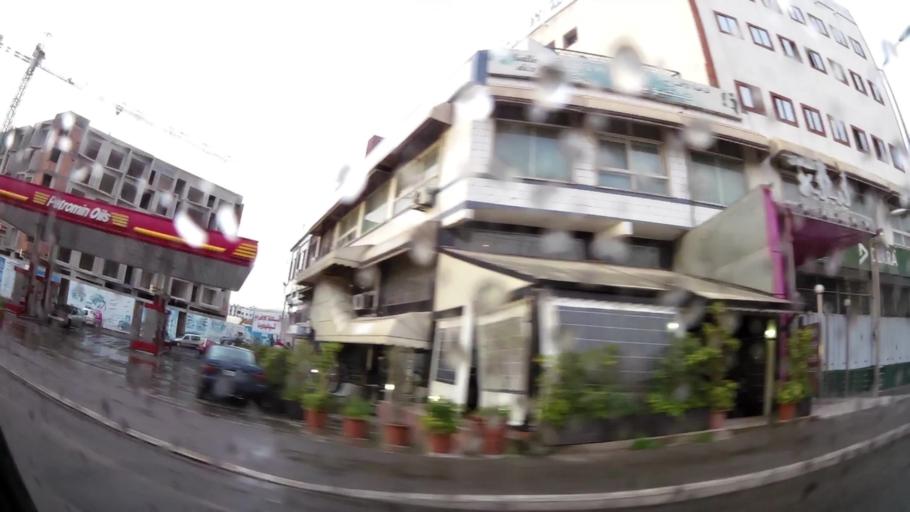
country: MA
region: Grand Casablanca
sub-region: Casablanca
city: Casablanca
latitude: 33.5779
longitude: -7.5527
